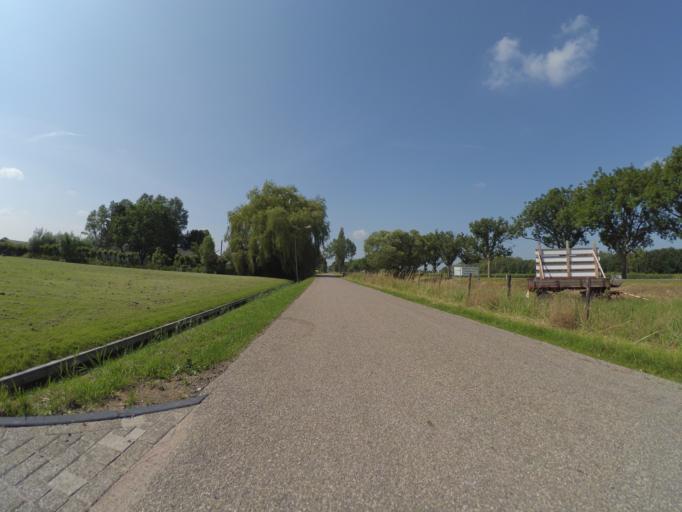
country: NL
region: South Holland
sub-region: Gemeente Leerdam
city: Leerdam
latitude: 51.9349
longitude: 5.1309
